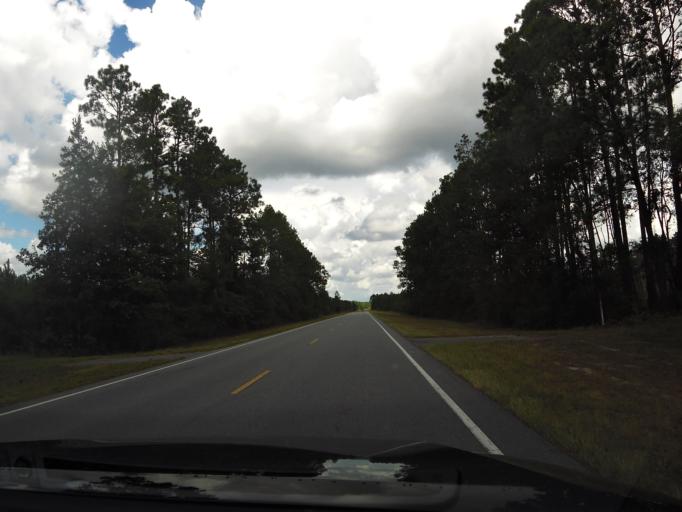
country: US
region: Georgia
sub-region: Charlton County
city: Folkston
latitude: 30.9207
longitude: -82.0203
